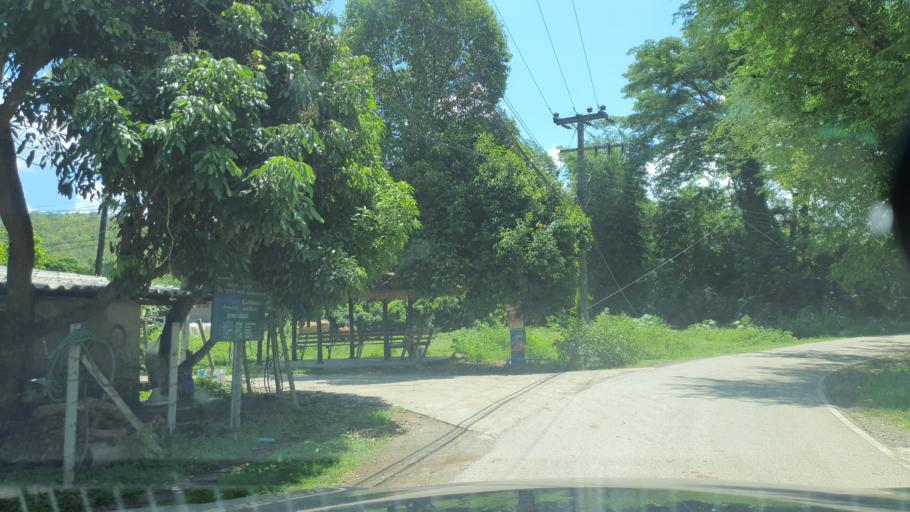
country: TH
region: Chiang Mai
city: Mae On
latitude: 18.8157
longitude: 99.2607
